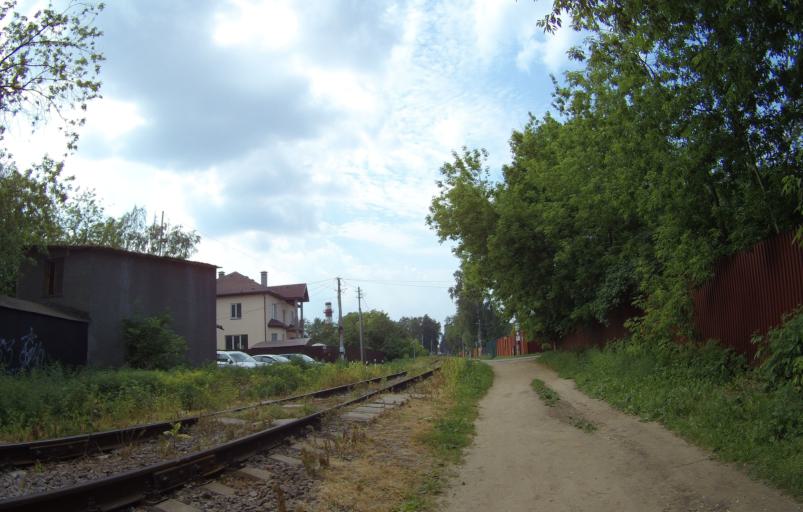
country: RU
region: Moskovskaya
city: Bykovo
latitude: 55.6206
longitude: 38.0731
